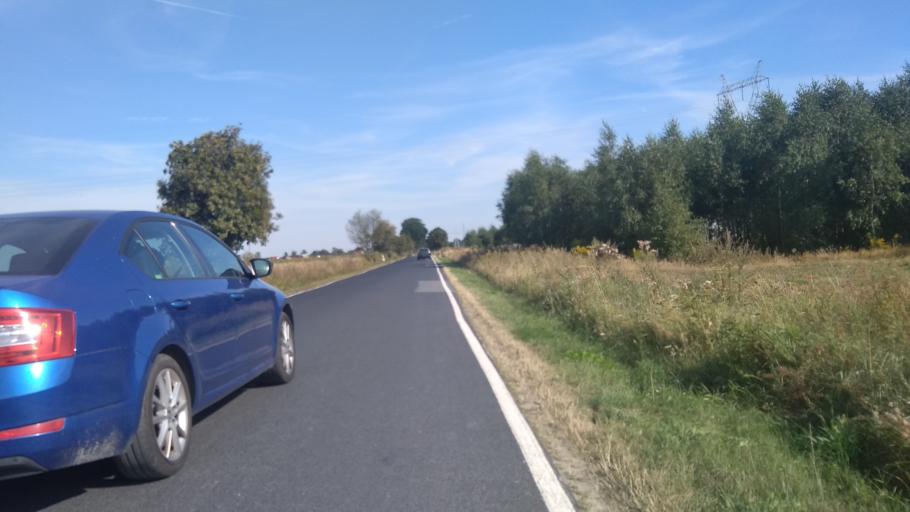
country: PL
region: Kujawsko-Pomorskie
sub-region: Powiat bydgoski
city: Osielsko
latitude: 53.2178
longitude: 18.1386
